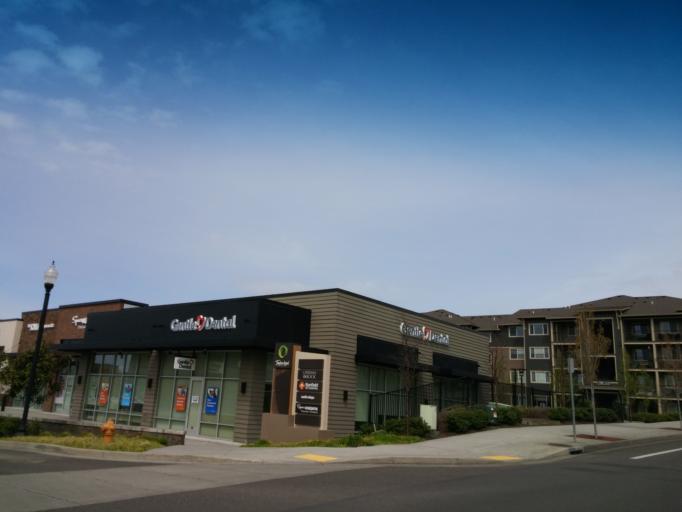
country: US
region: Oregon
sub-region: Washington County
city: Cedar Mill
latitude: 45.5211
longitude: -122.8006
